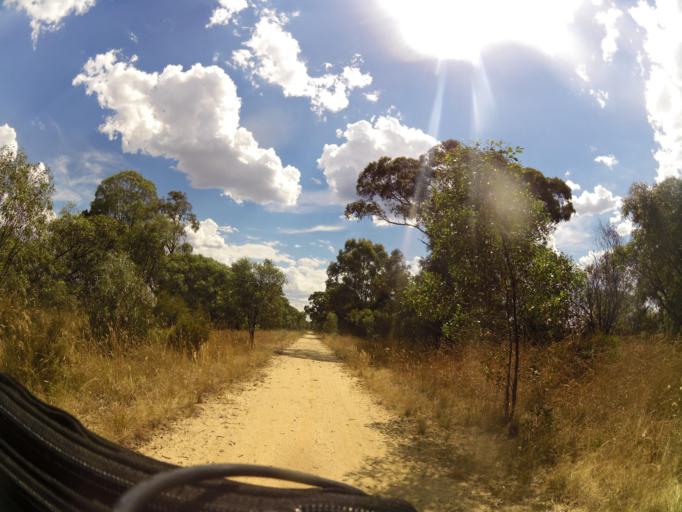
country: AU
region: Victoria
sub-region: Wellington
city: Heyfield
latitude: -37.9812
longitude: 146.7362
